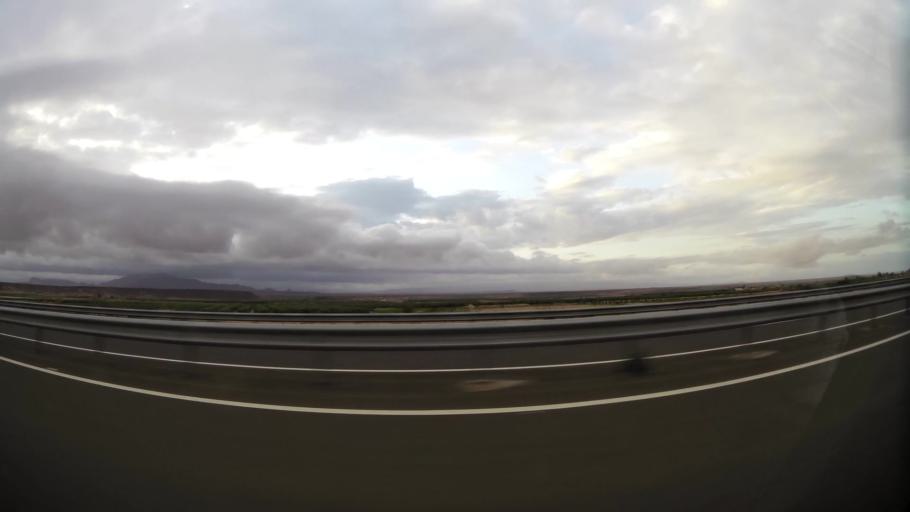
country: MA
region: Taza-Al Hoceima-Taounate
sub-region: Taza
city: Guercif
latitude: 34.4015
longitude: -3.1923
